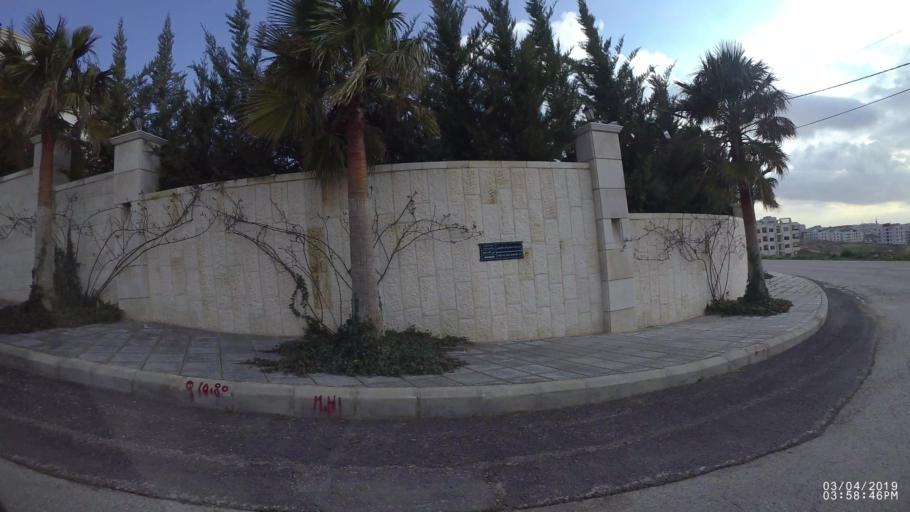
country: JO
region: Amman
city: Al Bunayyat ash Shamaliyah
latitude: 31.9112
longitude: 35.8729
